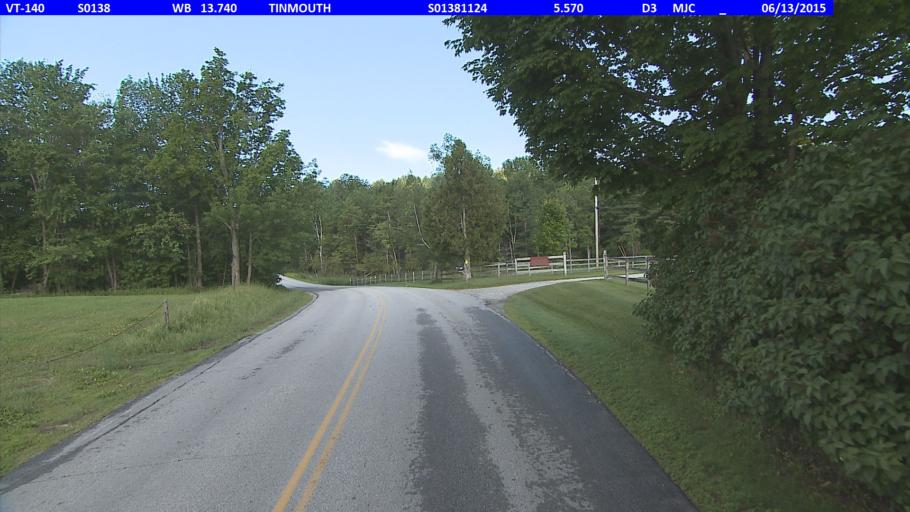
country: US
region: Vermont
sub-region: Rutland County
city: West Rutland
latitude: 43.4565
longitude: -73.0135
